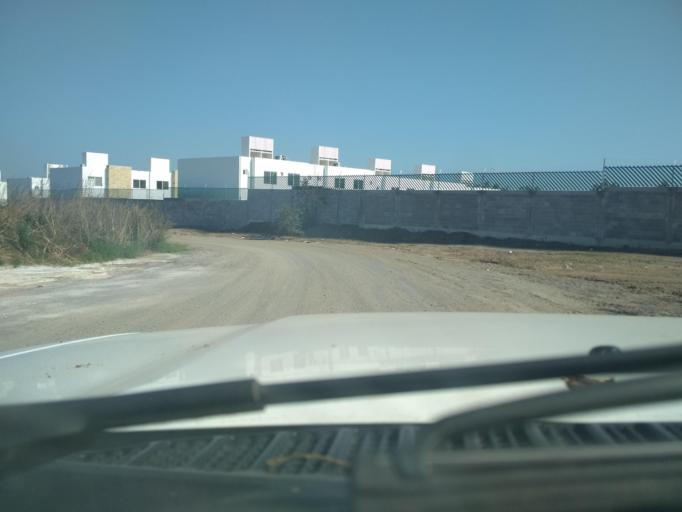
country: MX
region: Veracruz
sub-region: Veracruz
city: Las Amapolas
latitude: 19.1511
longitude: -96.2097
